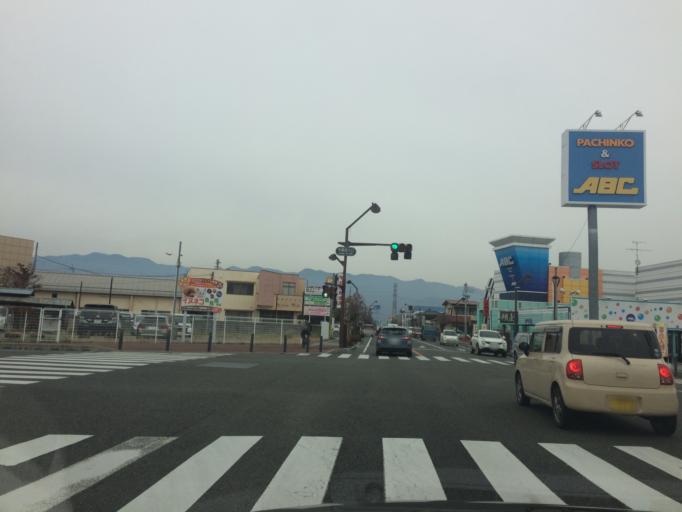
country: JP
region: Yamanashi
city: Kofu-shi
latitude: 35.6387
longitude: 138.5533
